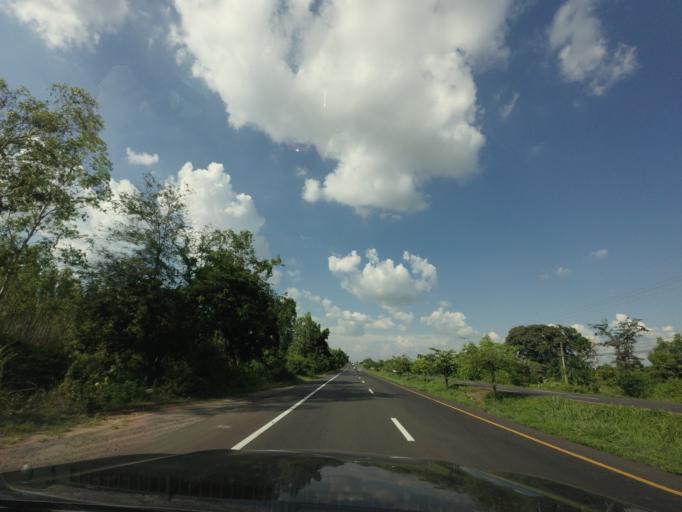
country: TH
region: Nakhon Ratchasima
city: Bua Lai
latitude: 15.6931
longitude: 102.5811
